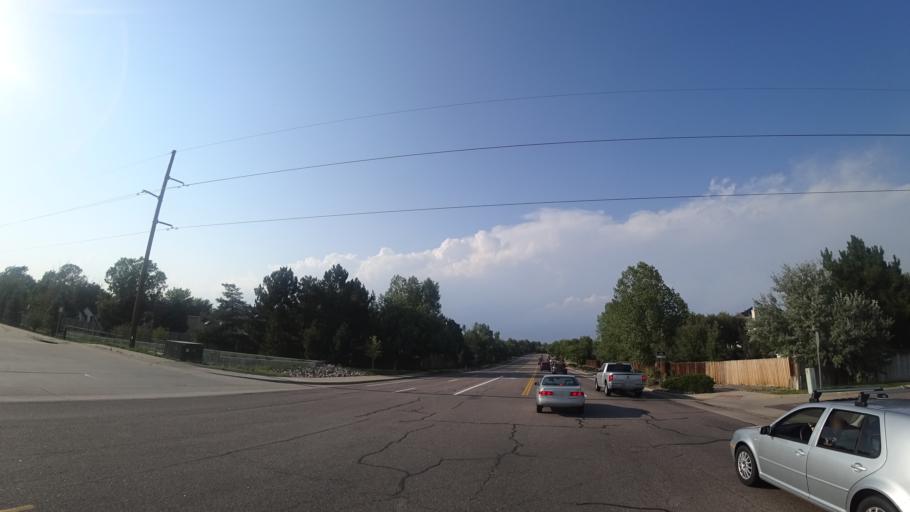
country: US
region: Colorado
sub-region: Arapahoe County
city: Dove Valley
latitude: 39.6091
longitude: -104.7447
